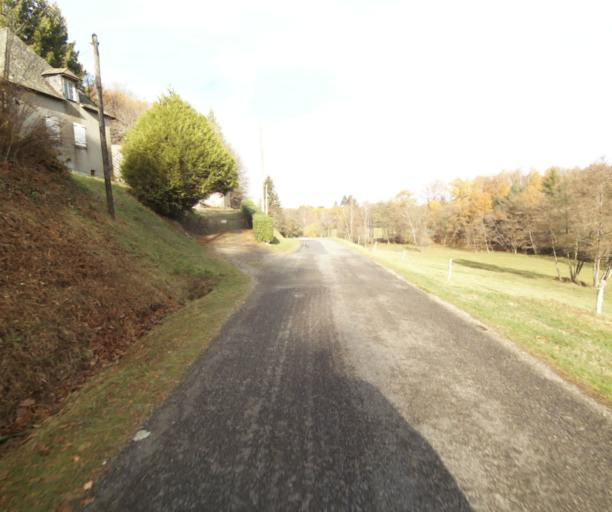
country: FR
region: Limousin
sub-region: Departement de la Correze
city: Sainte-Fortunade
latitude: 45.1920
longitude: 1.7383
